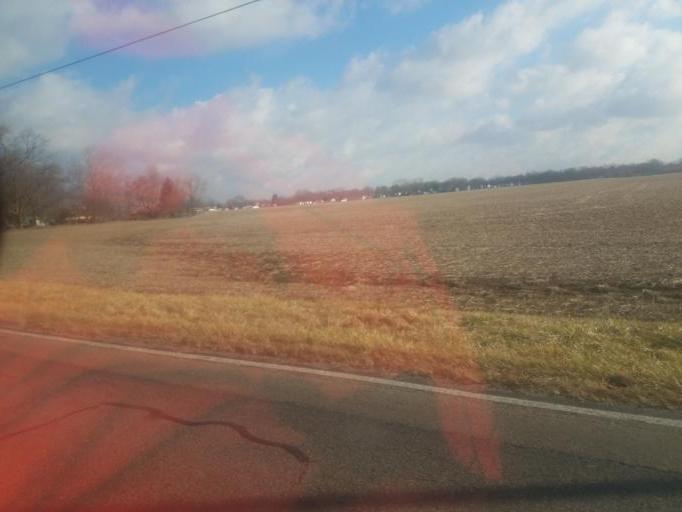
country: US
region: Ohio
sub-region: Marion County
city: Marion
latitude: 40.5803
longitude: -83.1644
